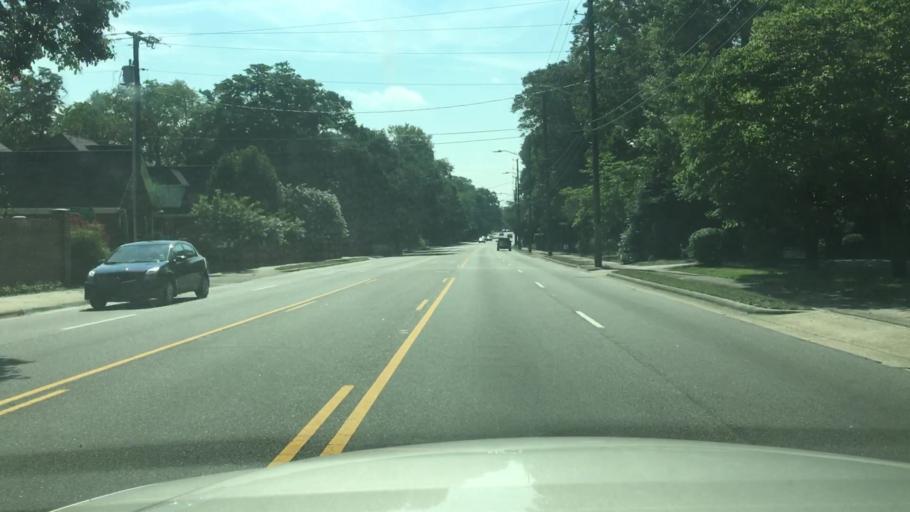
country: US
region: North Carolina
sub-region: Cumberland County
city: Fayetteville
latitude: 35.0595
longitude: -78.9105
